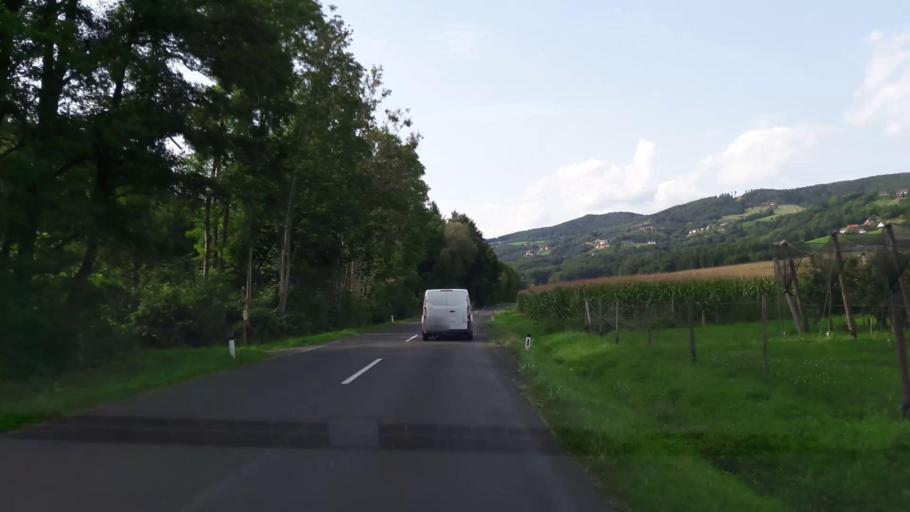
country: AT
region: Styria
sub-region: Politischer Bezirk Hartberg-Fuerstenfeld
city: Kaibing
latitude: 47.2276
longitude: 15.8463
